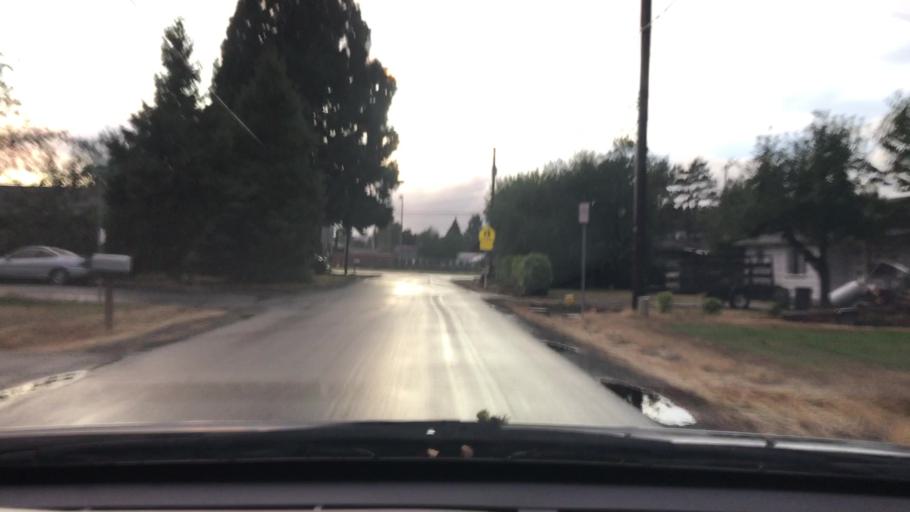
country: US
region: Oregon
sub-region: Yamhill County
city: McMinnville
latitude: 45.1981
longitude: -123.1942
